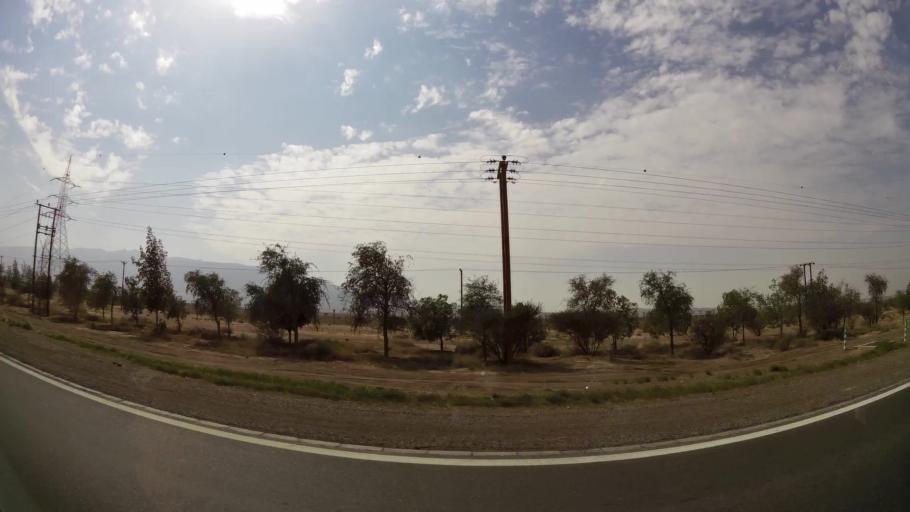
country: AE
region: Abu Dhabi
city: Al Ain
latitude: 24.1193
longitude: 55.8233
